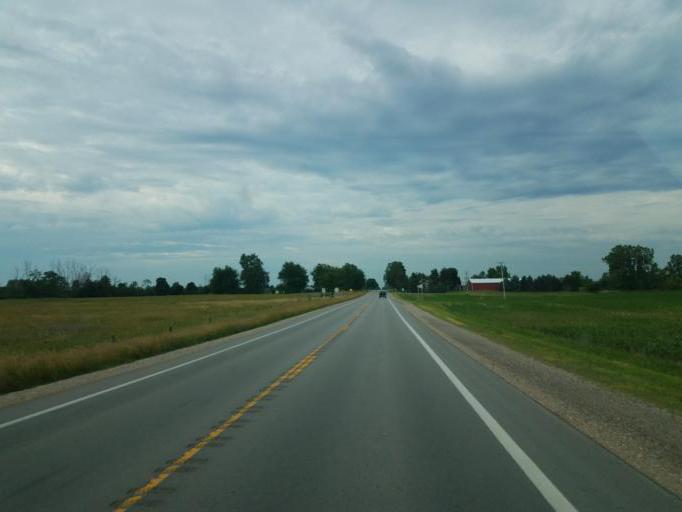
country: US
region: Michigan
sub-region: Eaton County
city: Charlotte
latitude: 42.6047
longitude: -84.8363
